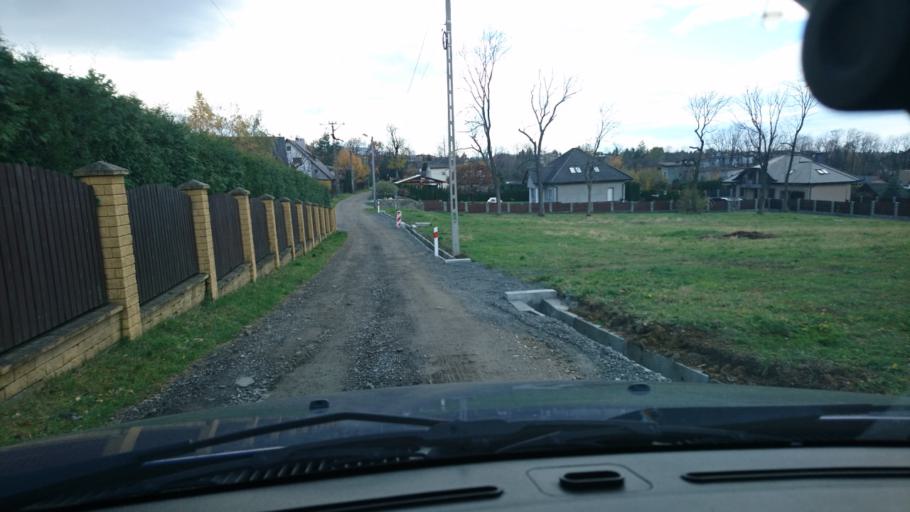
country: PL
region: Silesian Voivodeship
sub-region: Powiat bielski
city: Kozy
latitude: 49.8270
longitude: 19.1246
